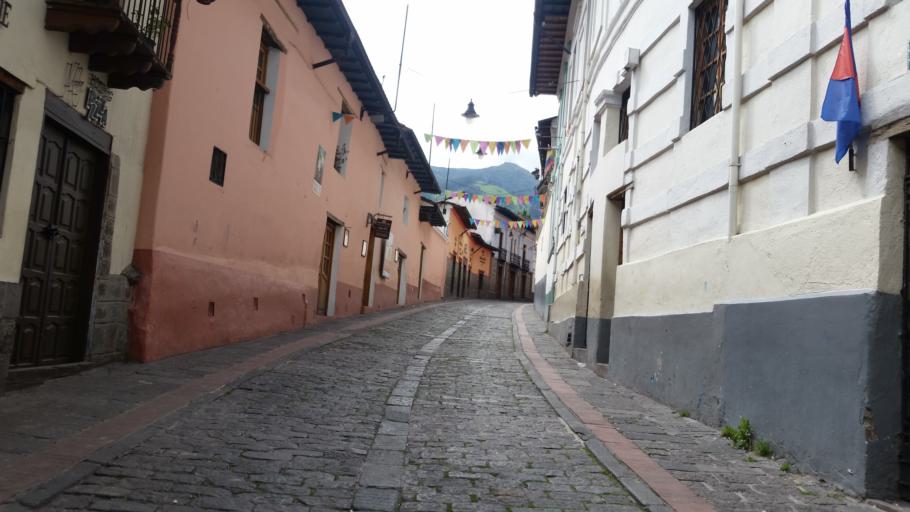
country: EC
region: Pichincha
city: Quito
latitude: -0.2256
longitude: -78.5133
